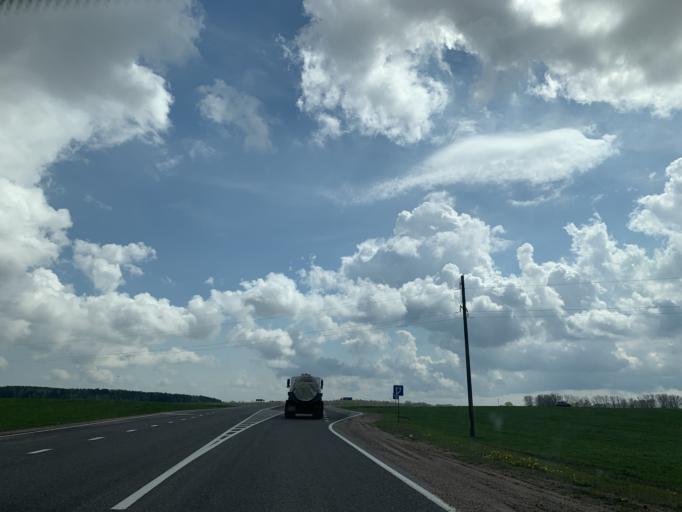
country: BY
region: Minsk
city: Nyasvizh
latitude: 53.2515
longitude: 26.6845
